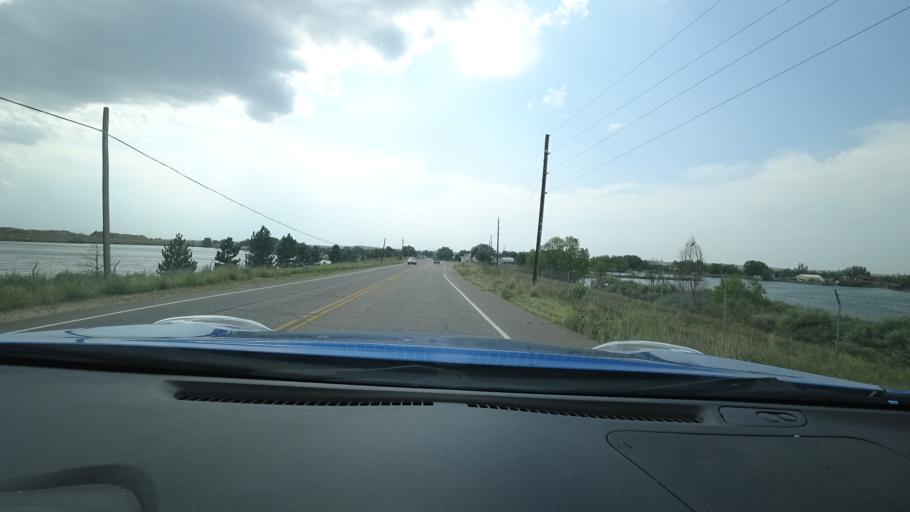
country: US
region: Colorado
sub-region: Adams County
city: Todd Creek
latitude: 39.9216
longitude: -104.8579
